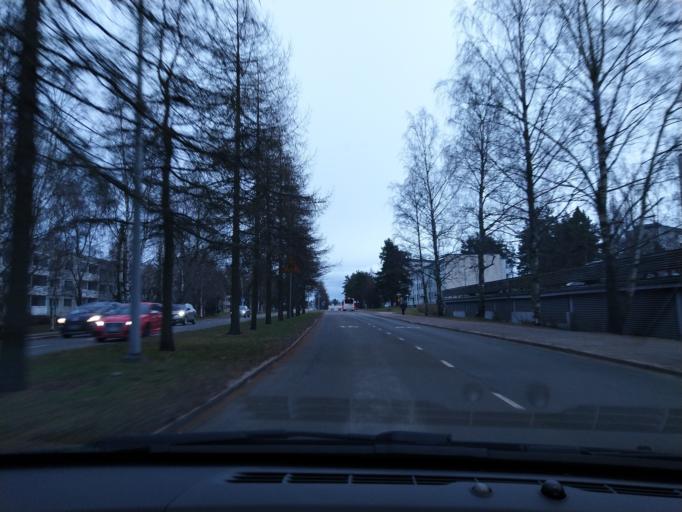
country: FI
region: Uusimaa
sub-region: Helsinki
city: Vantaa
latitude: 60.2391
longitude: 25.0753
